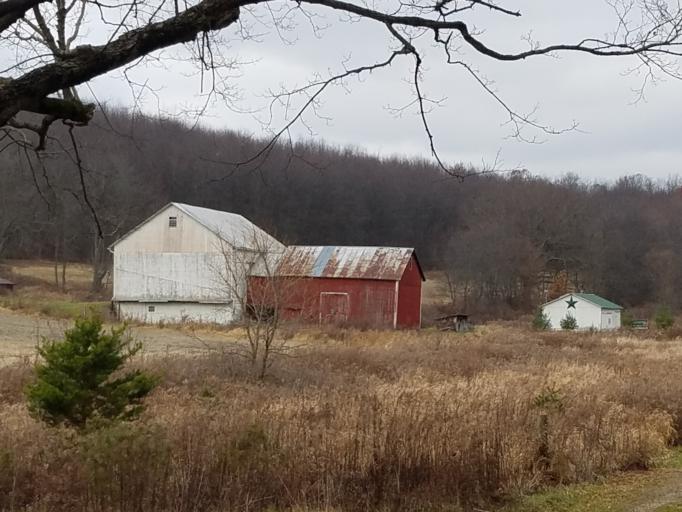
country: US
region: Ohio
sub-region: Sandusky County
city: Bellville
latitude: 40.5629
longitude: -82.3874
